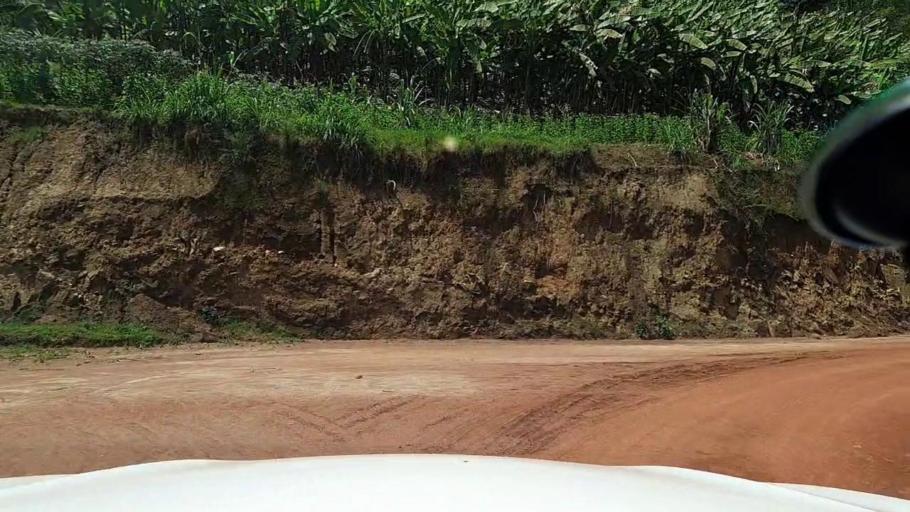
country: RW
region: Northern Province
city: Musanze
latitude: -1.6951
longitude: 29.8206
